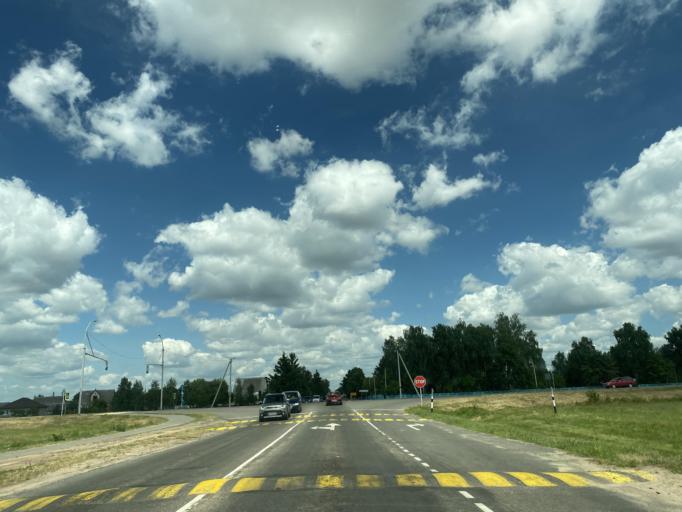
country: BY
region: Brest
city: Ivanava
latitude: 52.1573
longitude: 25.5450
